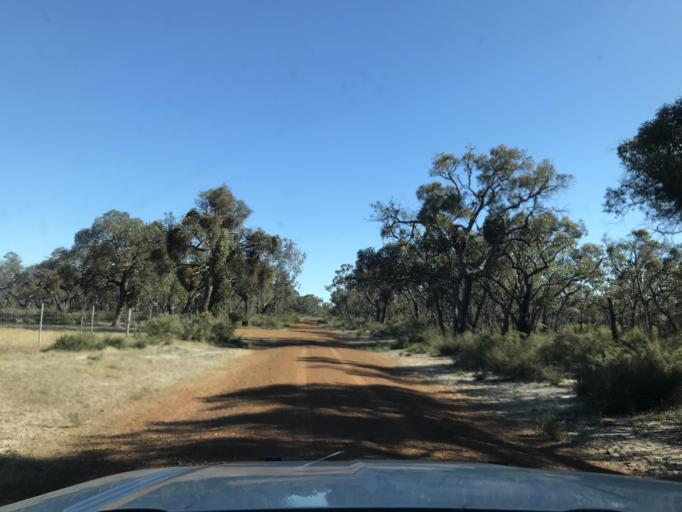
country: AU
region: South Australia
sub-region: Wattle Range
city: Penola
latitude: -37.0826
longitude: 141.3997
